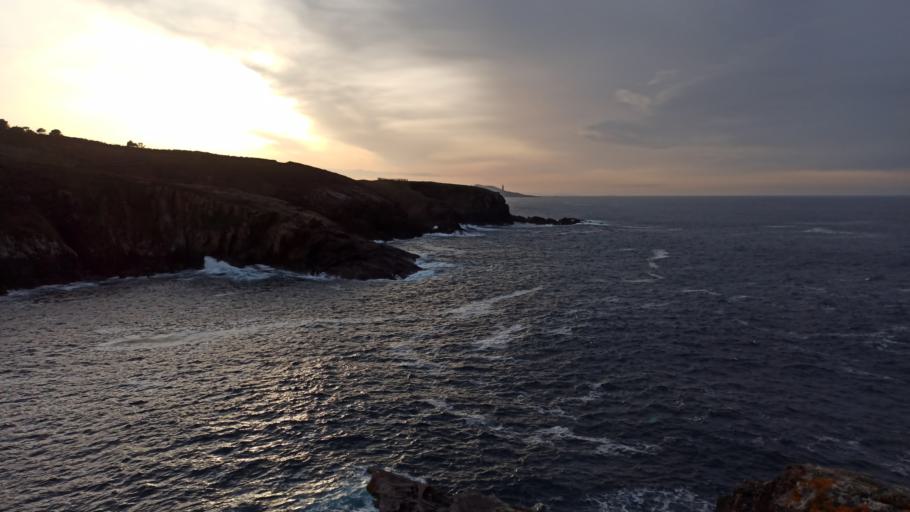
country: ES
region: Galicia
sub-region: Provincia da Coruna
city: A Coruna
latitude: 43.3996
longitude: -8.3370
